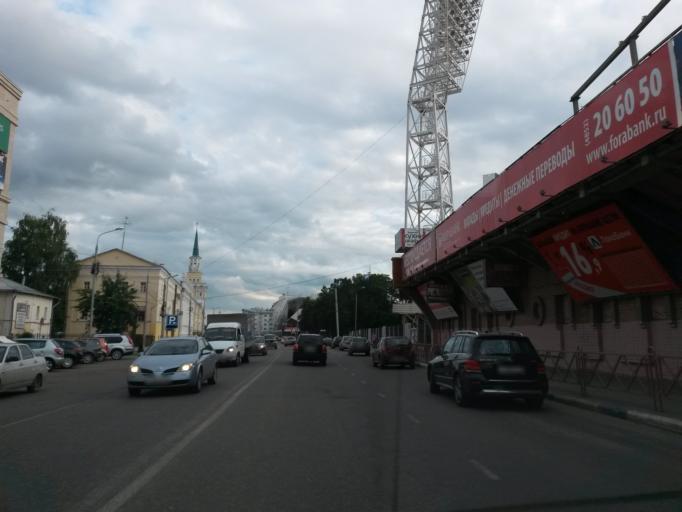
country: RU
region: Jaroslavl
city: Yaroslavl
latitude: 57.6283
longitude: 39.8686
